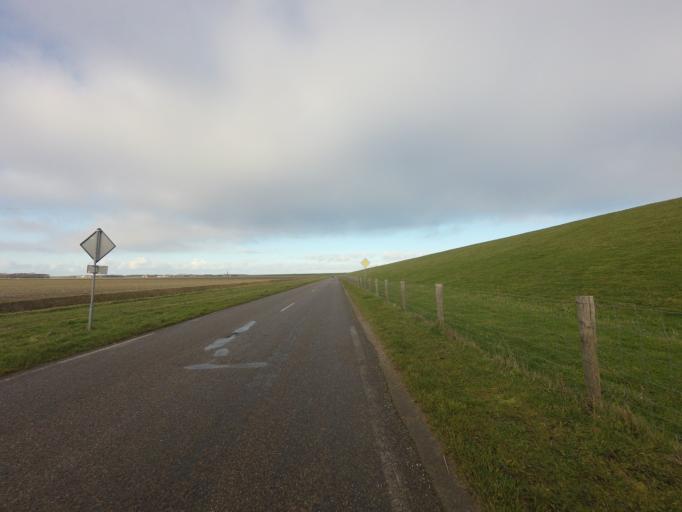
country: NL
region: North Holland
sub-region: Gemeente Texel
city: Den Burg
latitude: 53.1594
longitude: 4.8763
